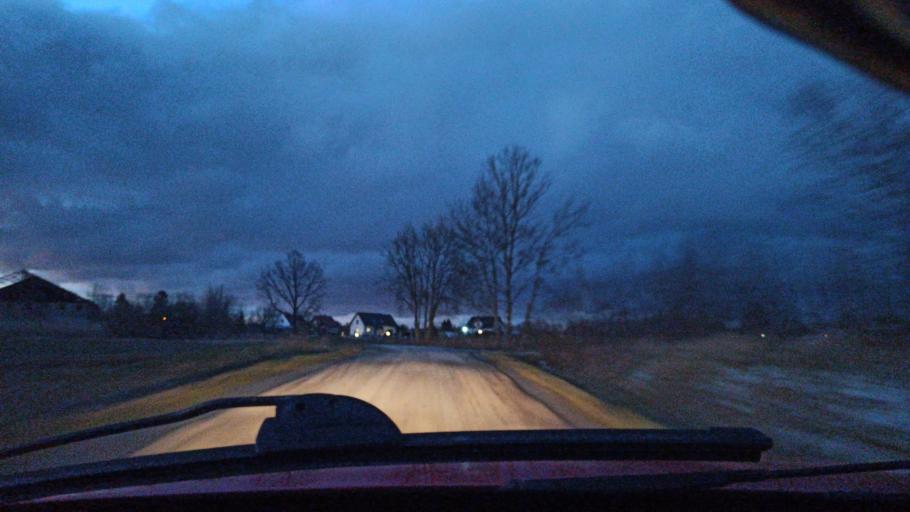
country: PL
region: Warmian-Masurian Voivodeship
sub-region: Powiat elblaski
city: Gronowo Gorne
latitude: 54.1788
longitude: 19.5421
